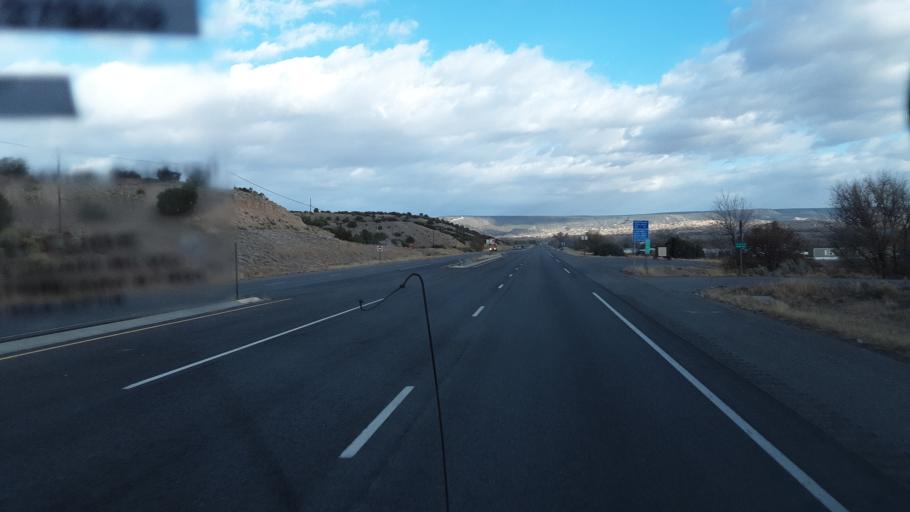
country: US
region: New Mexico
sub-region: Rio Arriba County
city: Ohkay Owingeh
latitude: 36.0272
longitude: -106.0925
